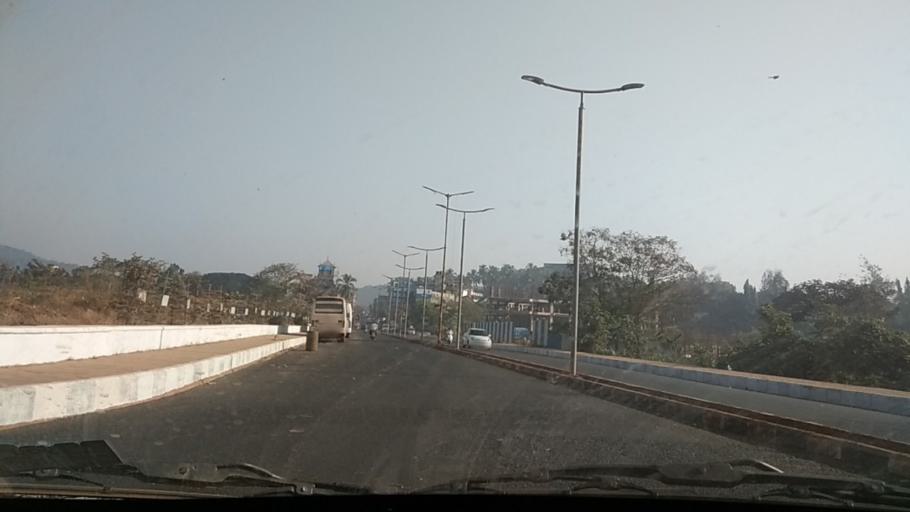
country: IN
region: Goa
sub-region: South Goa
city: Curchorem
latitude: 15.2589
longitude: 74.1055
